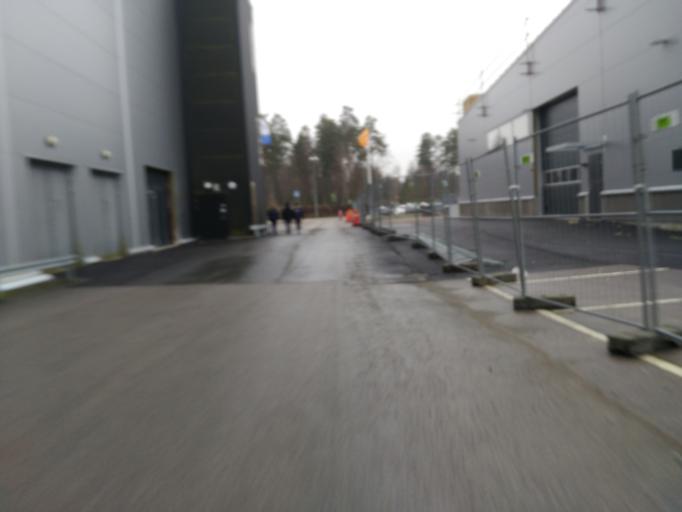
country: SE
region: Vaestra Goetaland
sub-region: Lidkopings Kommun
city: Lidkoping
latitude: 58.4946
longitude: 13.1417
